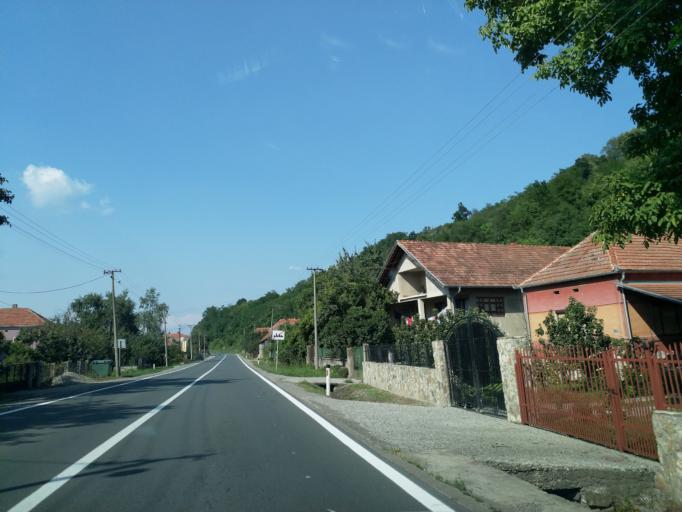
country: RS
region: Central Serbia
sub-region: Rasinski Okrug
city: Varvarin
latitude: 43.6580
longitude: 21.3847
